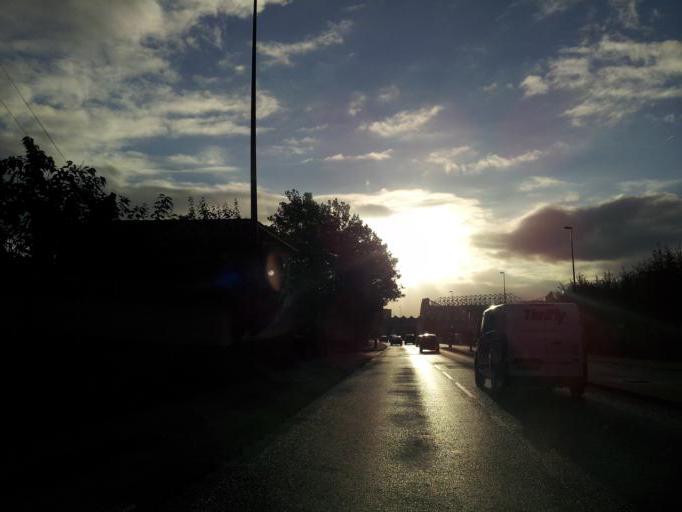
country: GB
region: England
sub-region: Trafford
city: Trafford Park
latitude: 53.4667
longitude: -2.3013
